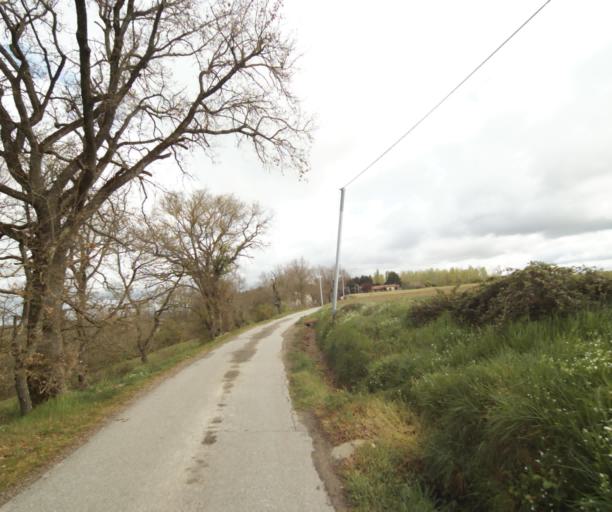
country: FR
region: Midi-Pyrenees
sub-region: Departement de l'Ariege
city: Saverdun
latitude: 43.2223
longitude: 1.5593
